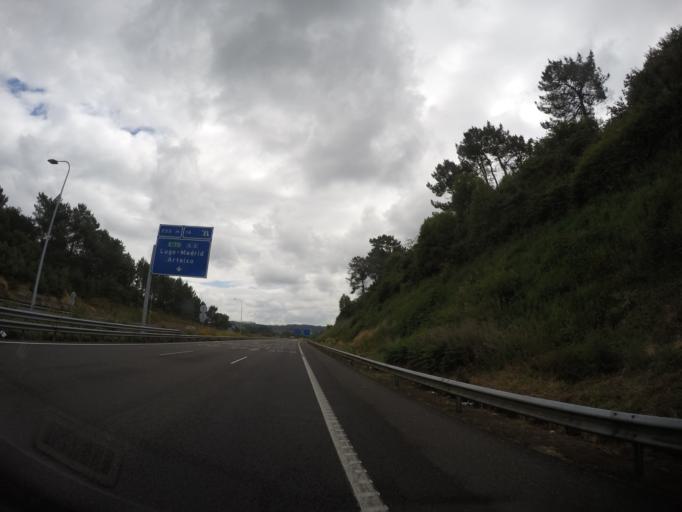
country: ES
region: Galicia
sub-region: Provincia da Coruna
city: Bergondo
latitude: 43.2810
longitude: -8.2704
